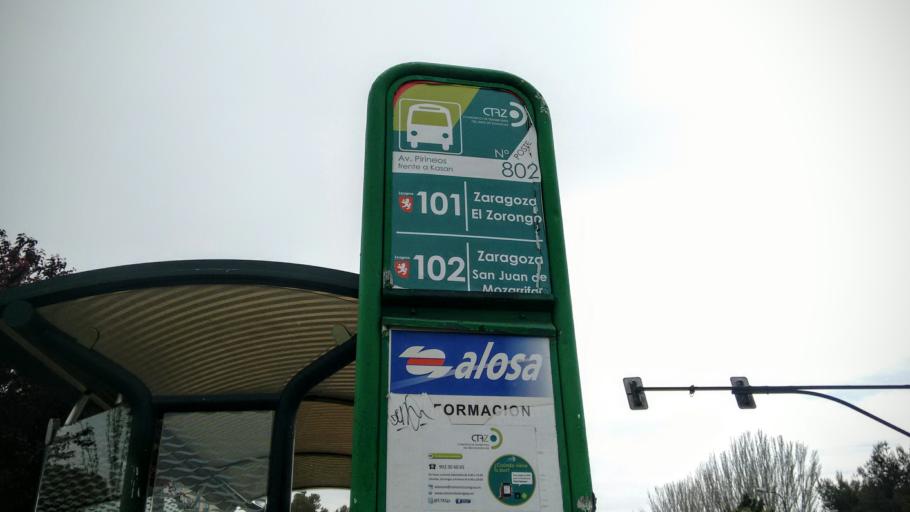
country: ES
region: Aragon
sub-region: Provincia de Zaragoza
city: Zaragoza
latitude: 41.6639
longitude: -0.8804
